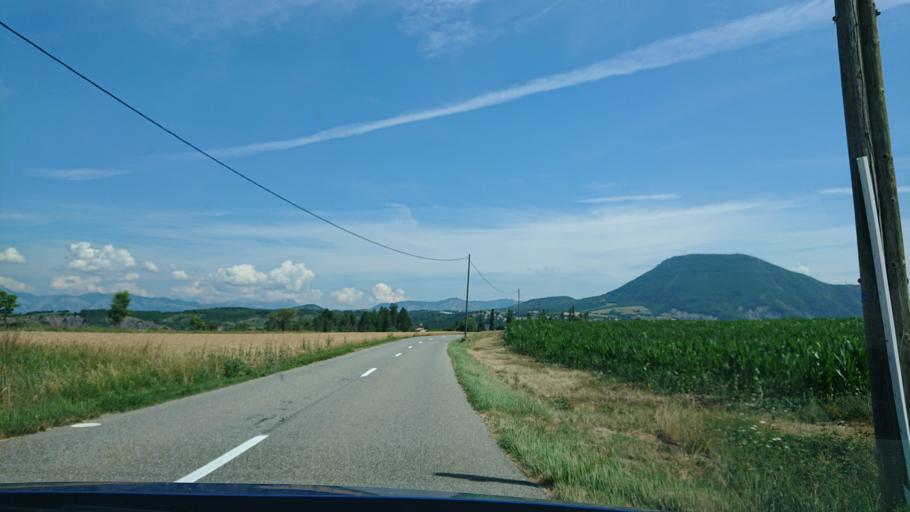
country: FR
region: Provence-Alpes-Cote d'Azur
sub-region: Departement des Alpes-de-Haute-Provence
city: Sisteron
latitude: 44.2432
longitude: 5.9484
